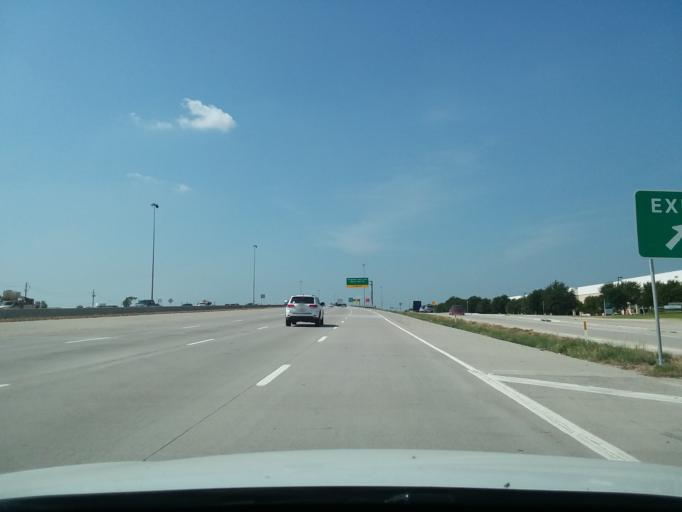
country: US
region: Texas
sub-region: Dallas County
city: Coppell
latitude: 32.9844
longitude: -97.0169
